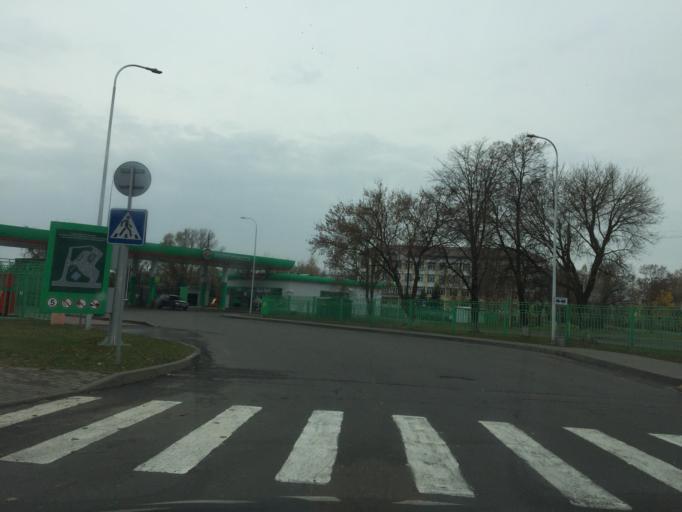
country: BY
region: Gomel
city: Dowsk
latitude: 53.1561
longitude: 30.4603
